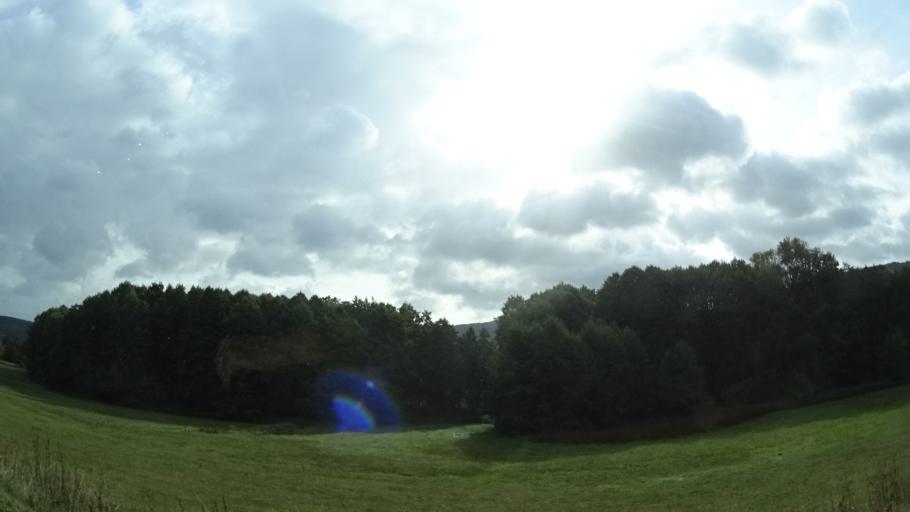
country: DE
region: Thuringia
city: Oberkatz
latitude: 50.6121
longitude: 10.2369
